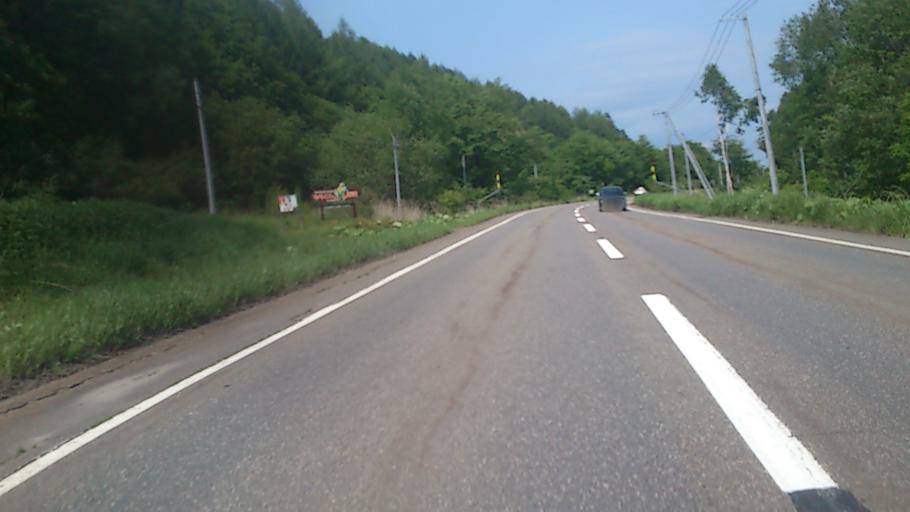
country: JP
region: Hokkaido
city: Otofuke
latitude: 43.2634
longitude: 143.5790
